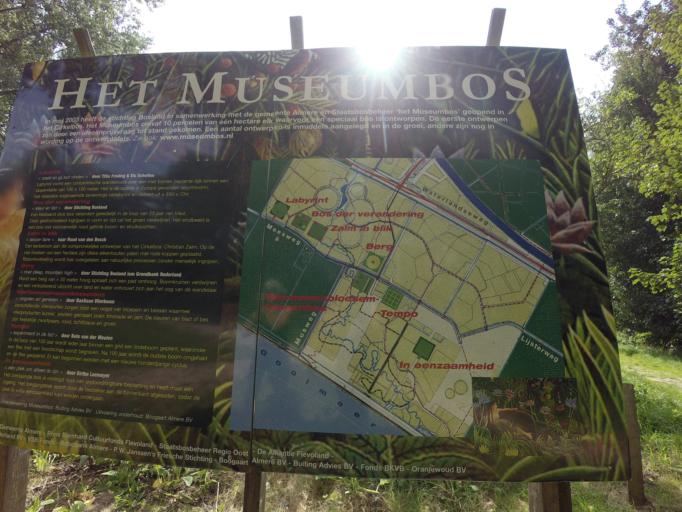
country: NL
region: North Holland
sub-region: Gemeente Huizen
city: Huizen
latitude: 52.3232
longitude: 5.2895
